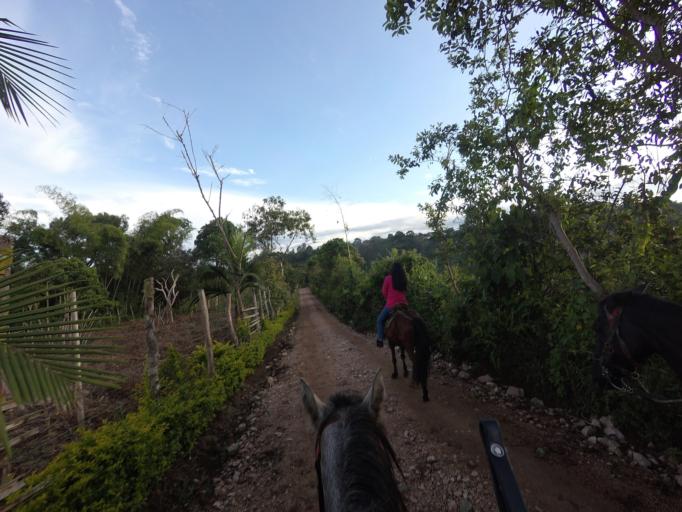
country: CO
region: Huila
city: San Agustin
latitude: 1.9011
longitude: -76.2731
